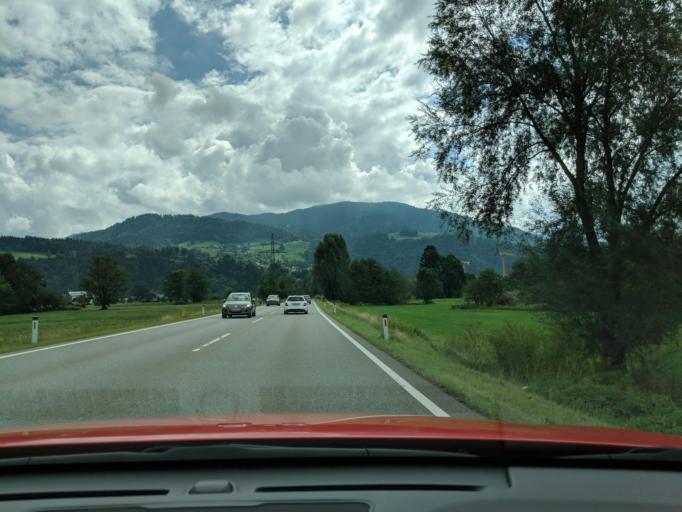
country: AT
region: Vorarlberg
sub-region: Politischer Bezirk Bregenz
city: Schwarzach
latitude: 47.4414
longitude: 9.7429
